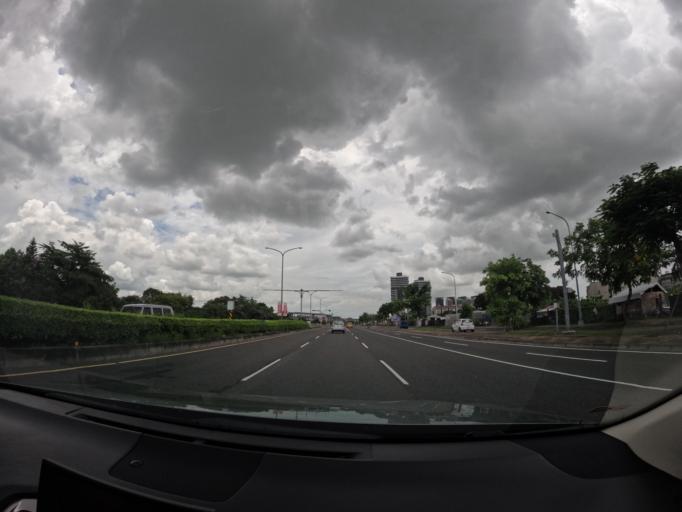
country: TW
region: Taiwan
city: Fengshan
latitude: 22.7487
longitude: 120.3148
